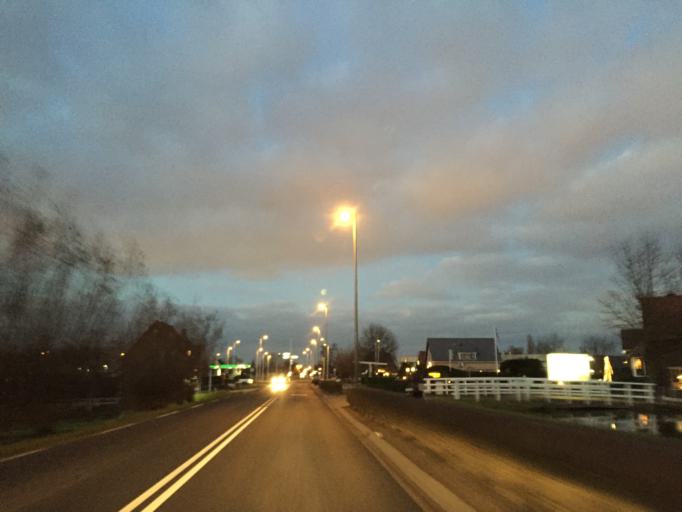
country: NL
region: South Holland
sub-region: Gemeente Lansingerland
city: Bergschenhoek
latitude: 51.9777
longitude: 4.4973
